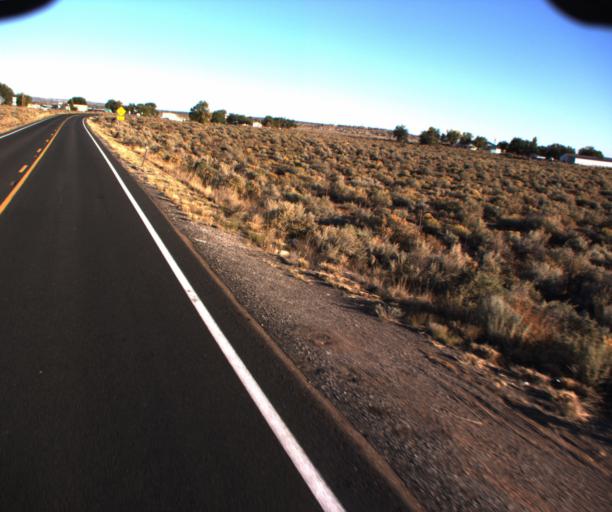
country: US
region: Arizona
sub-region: Apache County
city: Houck
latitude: 35.1936
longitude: -109.4373
